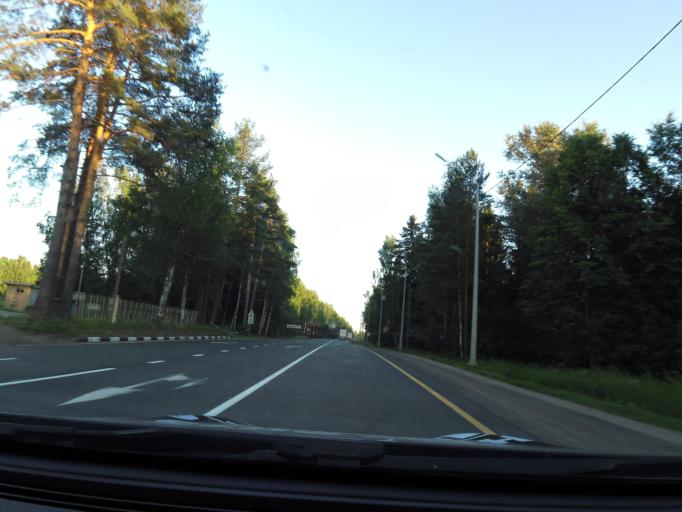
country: RU
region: Jaroslavl
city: Prechistoye
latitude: 58.4599
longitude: 40.3203
